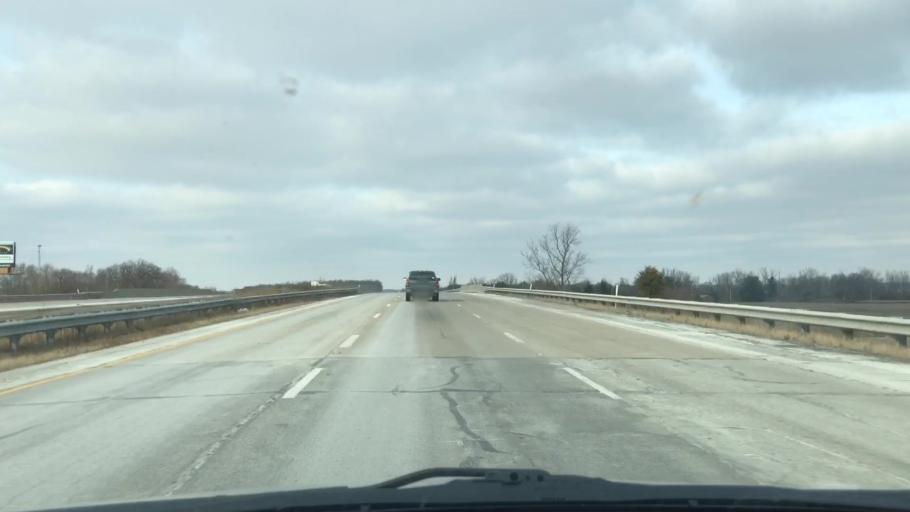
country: US
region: Indiana
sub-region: DeKalb County
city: Waterloo
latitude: 41.5297
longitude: -85.0555
